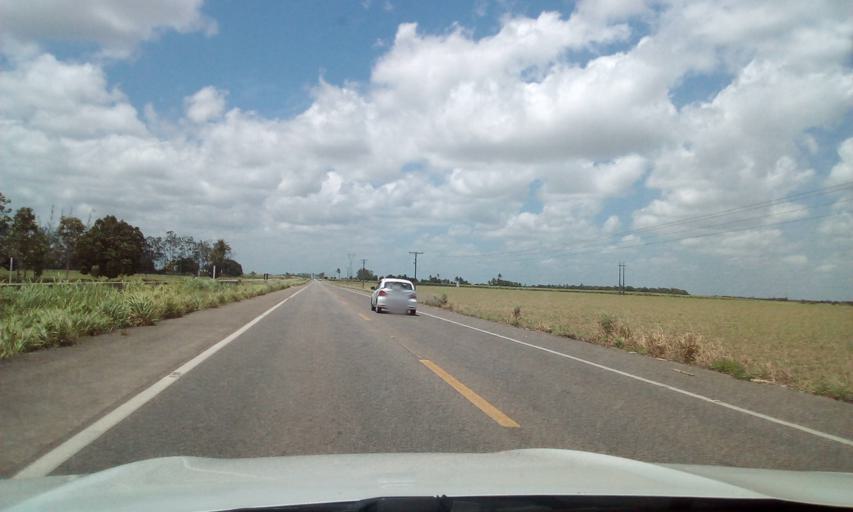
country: BR
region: Alagoas
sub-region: Campo Alegre
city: Campo Alegre
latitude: -9.9023
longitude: -36.2349
